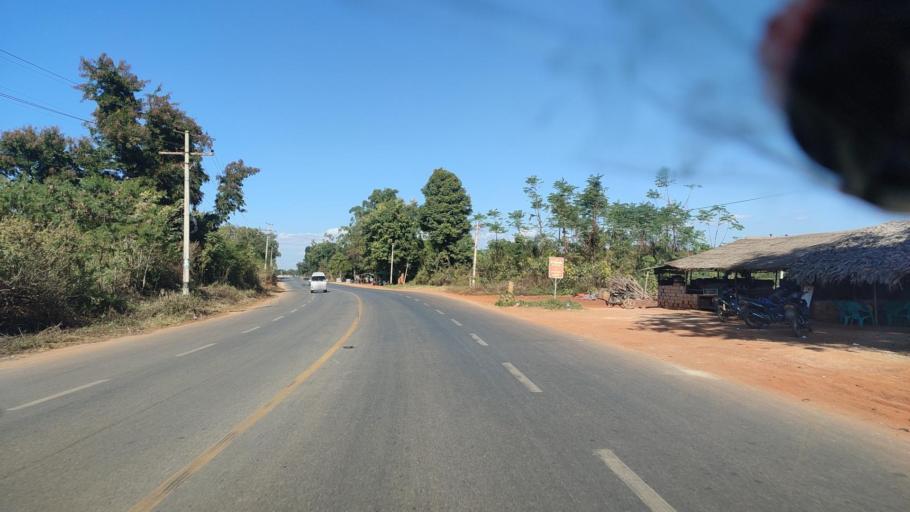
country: MM
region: Mandalay
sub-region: Pyin Oo Lwin District
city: Pyin Oo Lwin
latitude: 22.0972
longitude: 96.5970
